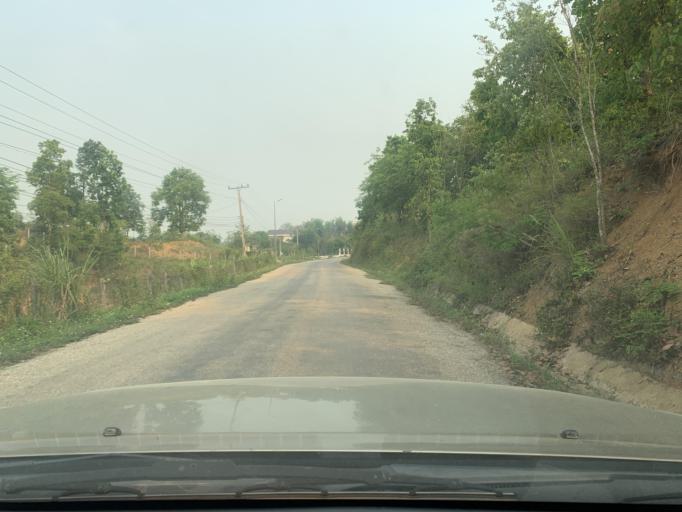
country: LA
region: Louangphabang
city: Louangphabang
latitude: 19.9094
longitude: 102.0836
